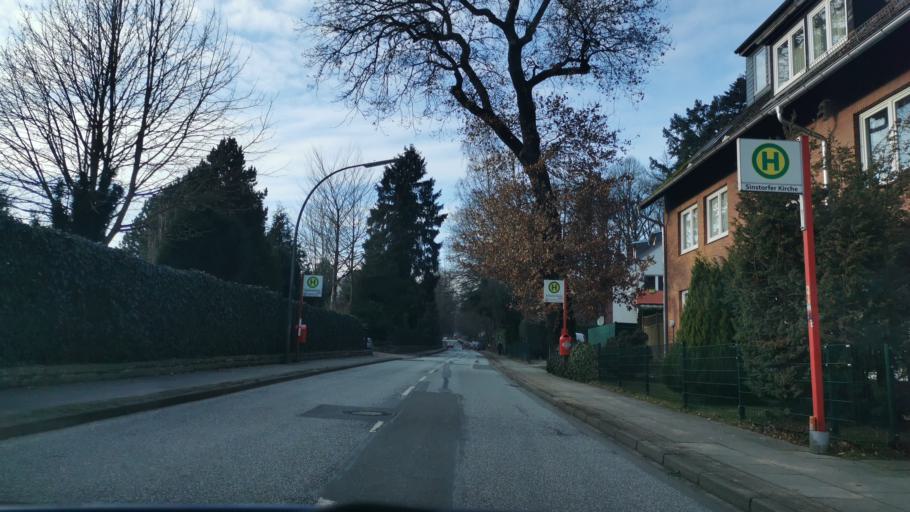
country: DE
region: Lower Saxony
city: Seevetal
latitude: 53.4242
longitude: 9.9738
